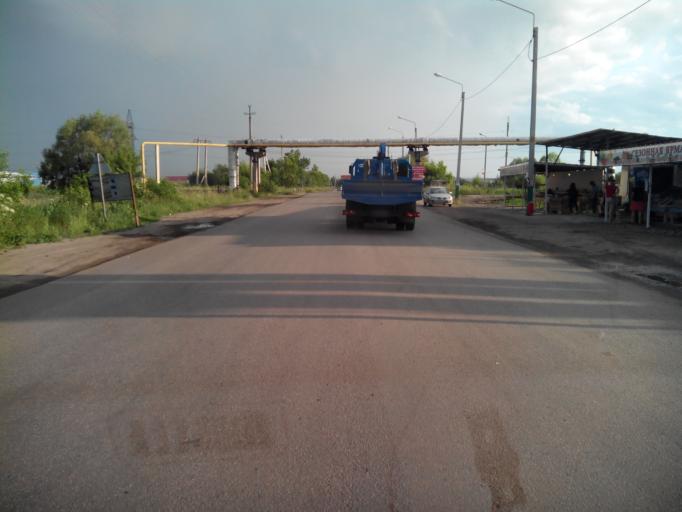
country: RU
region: Penza
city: Penza
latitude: 53.1308
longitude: 44.9977
